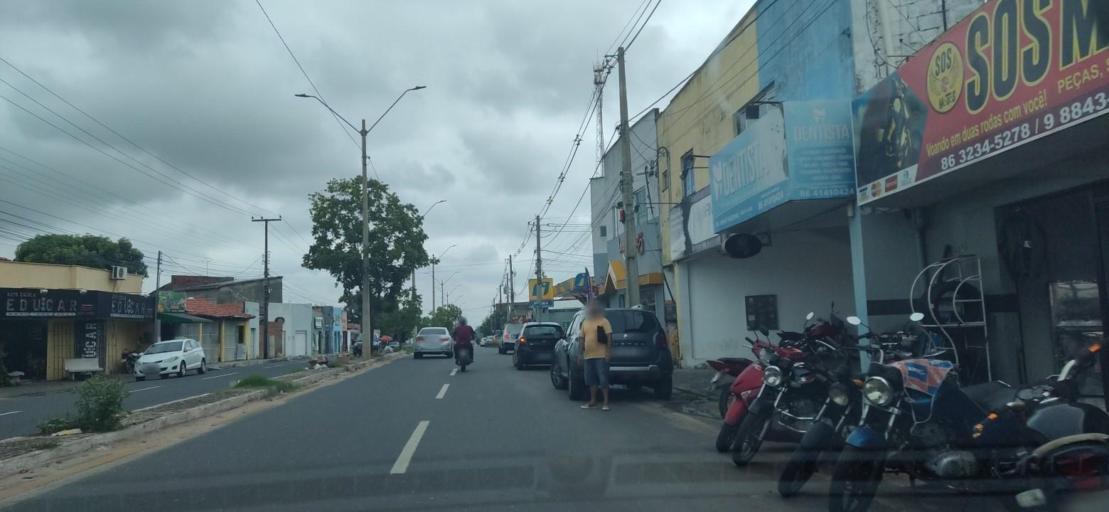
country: BR
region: Piaui
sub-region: Teresina
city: Teresina
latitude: -5.0515
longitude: -42.7419
